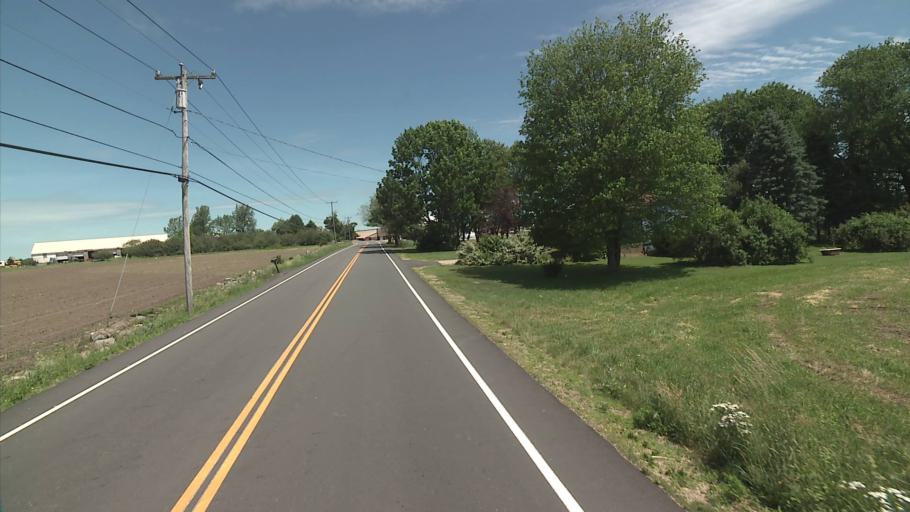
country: US
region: Connecticut
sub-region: Windham County
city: Moosup
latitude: 41.6476
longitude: -71.8472
